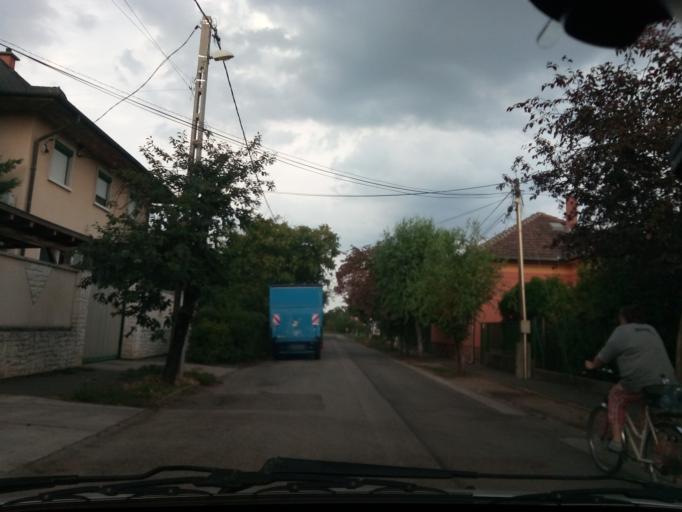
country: HU
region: Budapest
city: Budapest XVIII. keruelet
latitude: 47.4384
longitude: 19.1938
